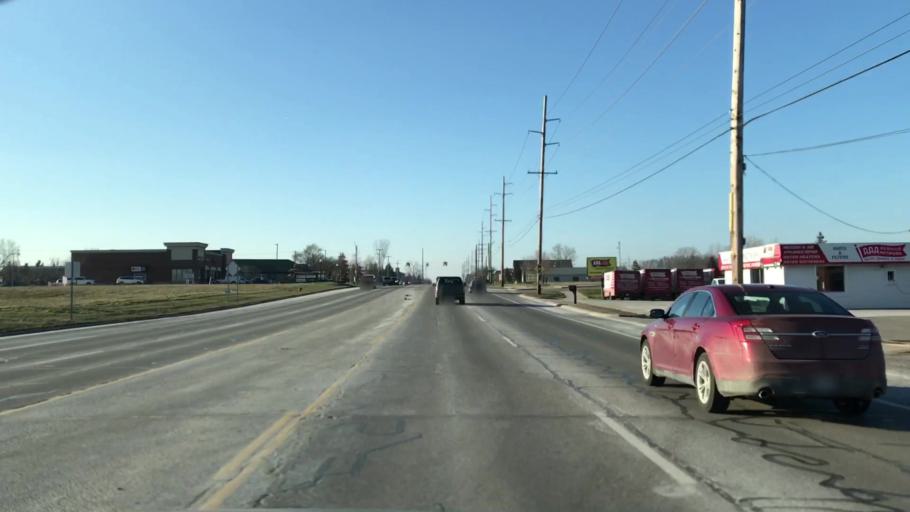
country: US
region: Michigan
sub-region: Livingston County
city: Howell
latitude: 42.5817
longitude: -83.8599
